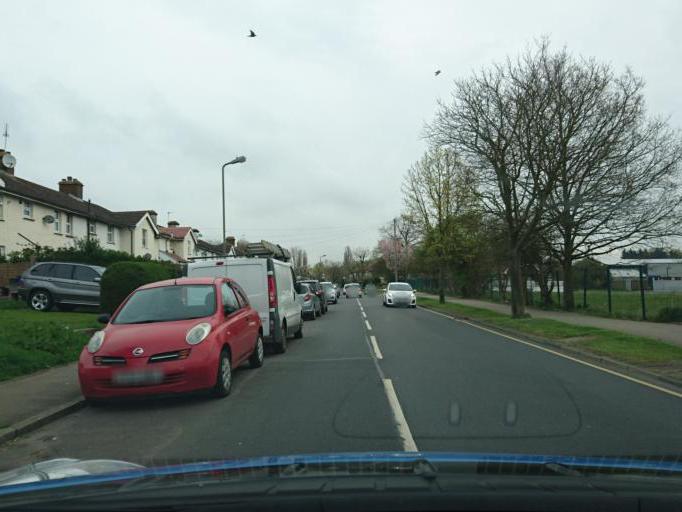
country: GB
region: England
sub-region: Greater London
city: Barnet
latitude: 51.6445
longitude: -0.1939
